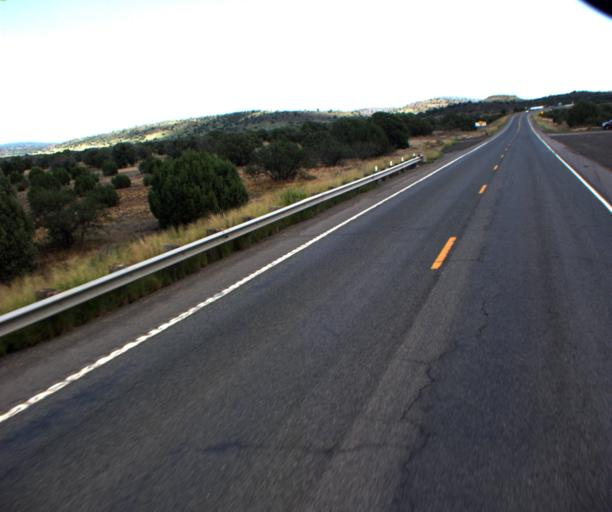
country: US
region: Arizona
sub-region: Yavapai County
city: Camp Verde
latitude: 34.5147
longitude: -112.0003
